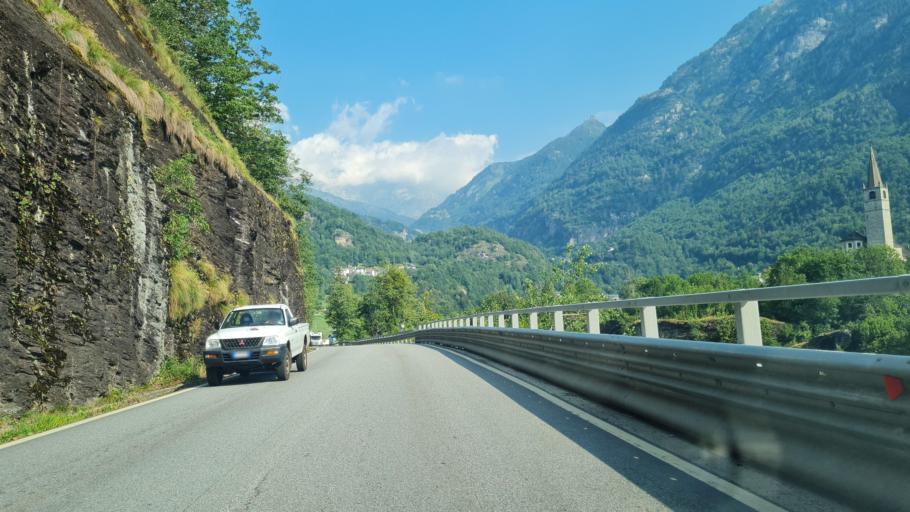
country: IT
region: Piedmont
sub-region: Provincia Verbano-Cusio-Ossola
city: Baceno
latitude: 46.2543
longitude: 8.3193
